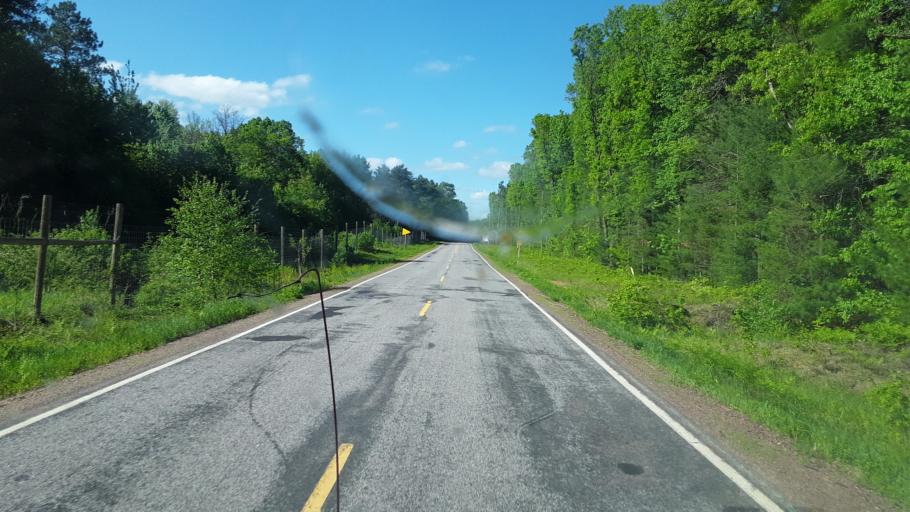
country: US
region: Wisconsin
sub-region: Wood County
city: Nekoosa
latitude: 44.3123
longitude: -90.1286
